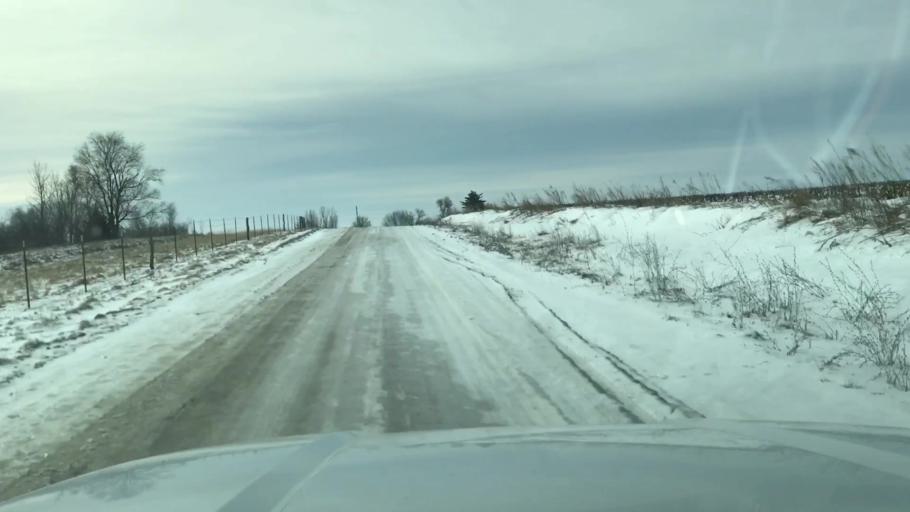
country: US
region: Missouri
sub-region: Holt County
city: Mound City
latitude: 40.1335
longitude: -95.0696
